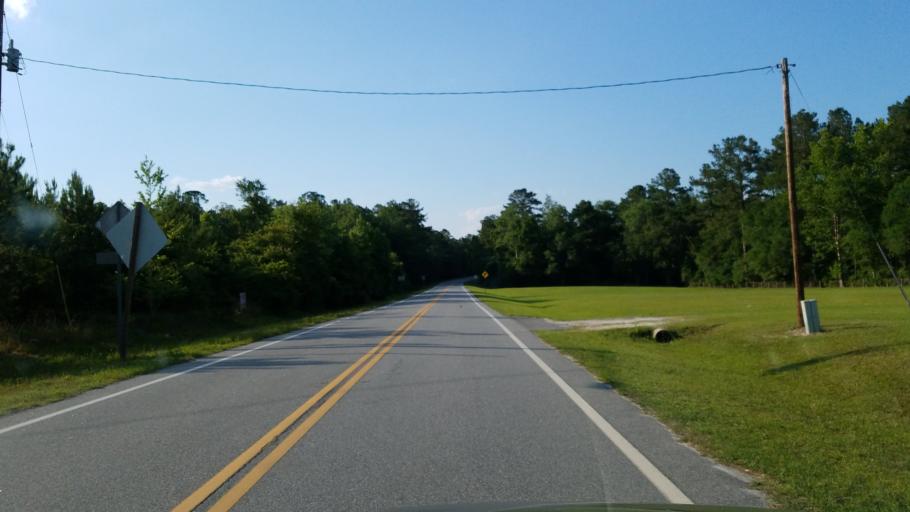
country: US
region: Georgia
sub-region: Echols County
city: Statenville
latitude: 30.8314
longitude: -83.0546
